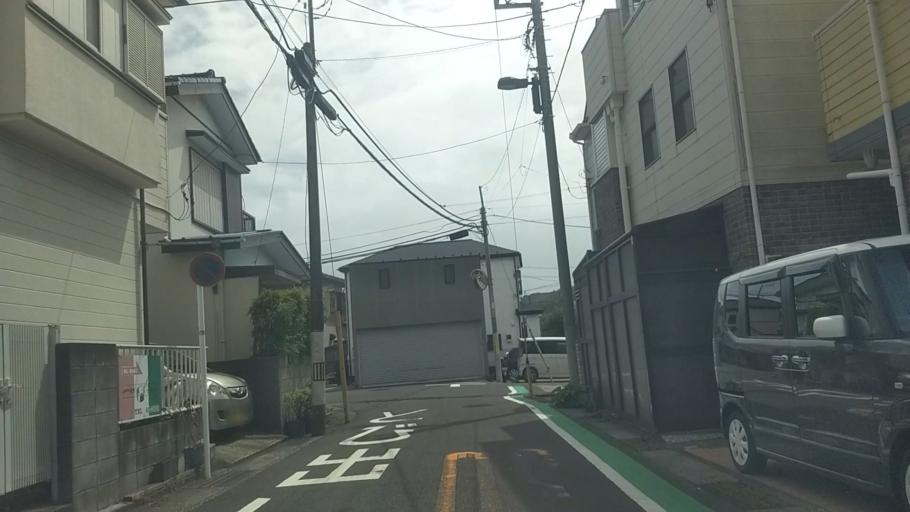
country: JP
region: Kanagawa
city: Yokosuka
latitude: 35.2437
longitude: 139.7215
